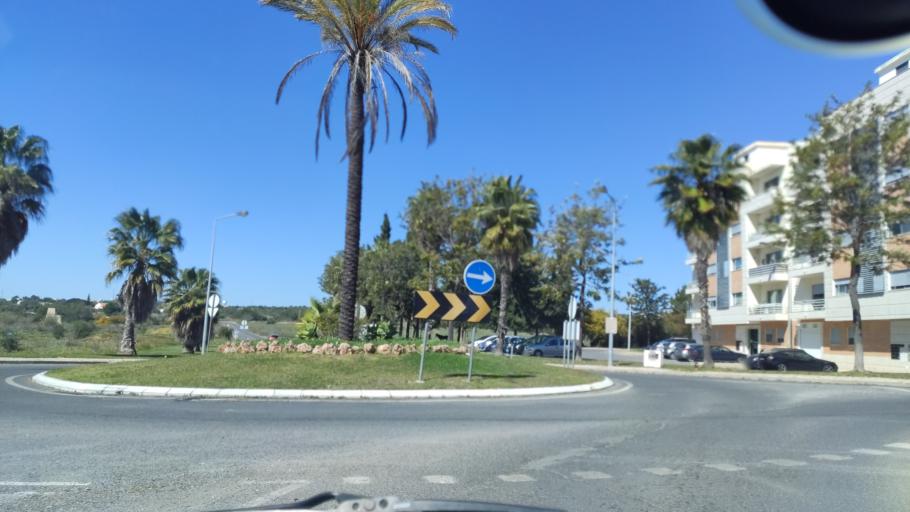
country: PT
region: Faro
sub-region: Olhao
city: Olhao
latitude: 37.0406
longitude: -7.8517
